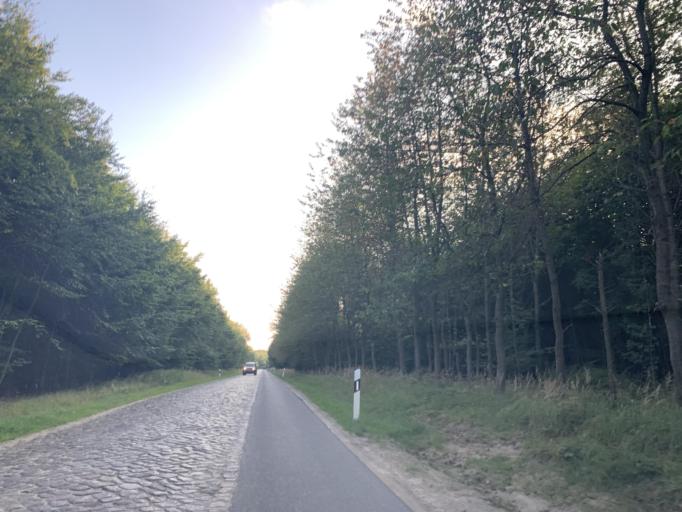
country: DE
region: Mecklenburg-Vorpommern
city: Loitz
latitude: 53.3583
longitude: 13.4339
